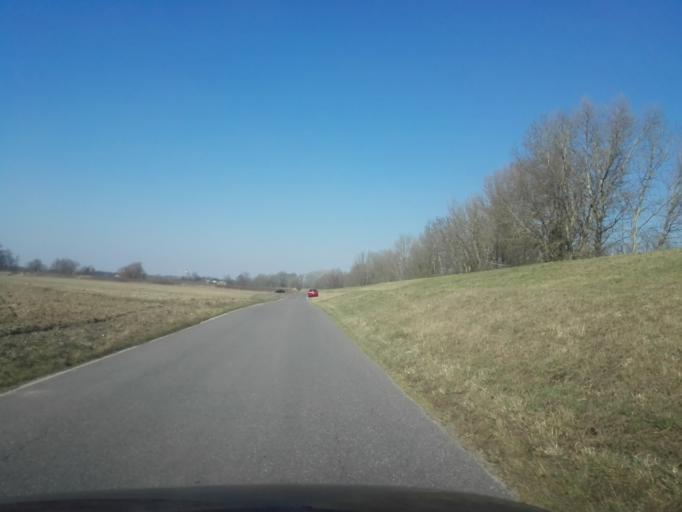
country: PL
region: Masovian Voivodeship
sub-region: Powiat piaseczynski
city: Konstancin-Jeziorna
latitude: 52.1324
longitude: 21.1673
